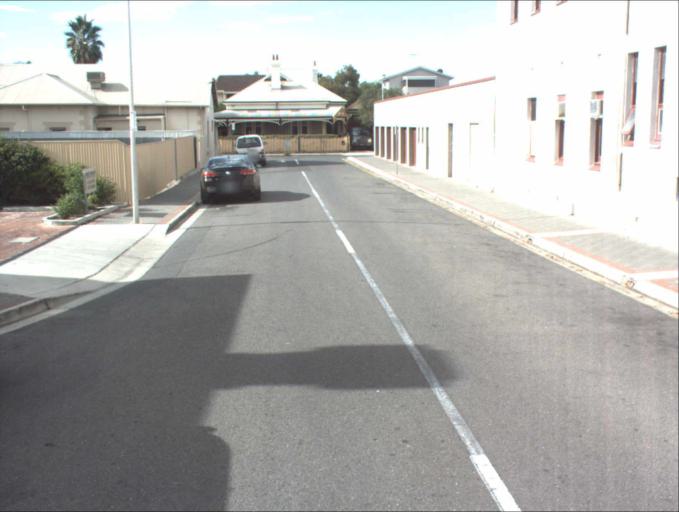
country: AU
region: South Australia
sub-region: Port Adelaide Enfield
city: Birkenhead
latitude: -34.8382
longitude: 138.4815
